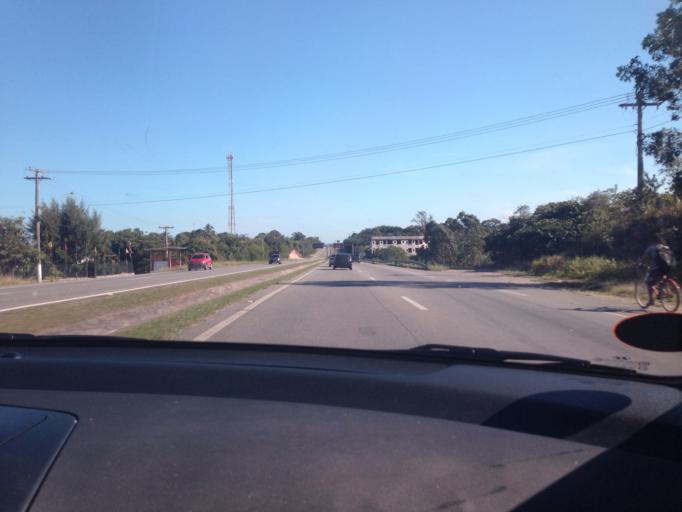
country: BR
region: Espirito Santo
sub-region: Viana
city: Viana
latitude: -20.5195
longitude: -40.3686
